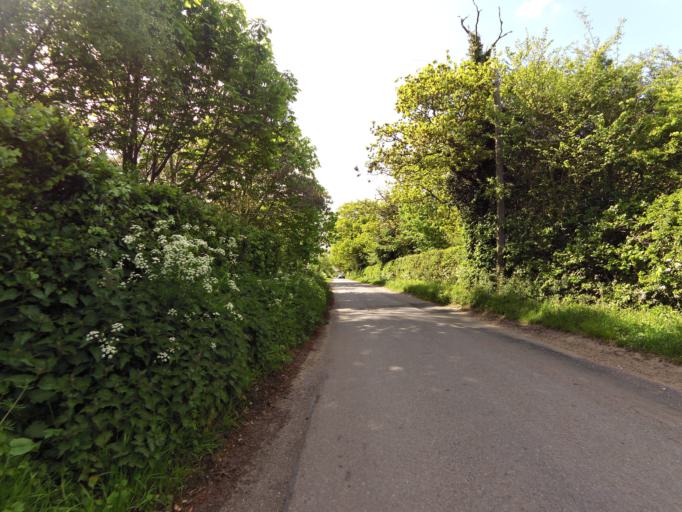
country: GB
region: England
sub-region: Suffolk
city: Wrentham
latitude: 52.4463
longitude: 1.6481
